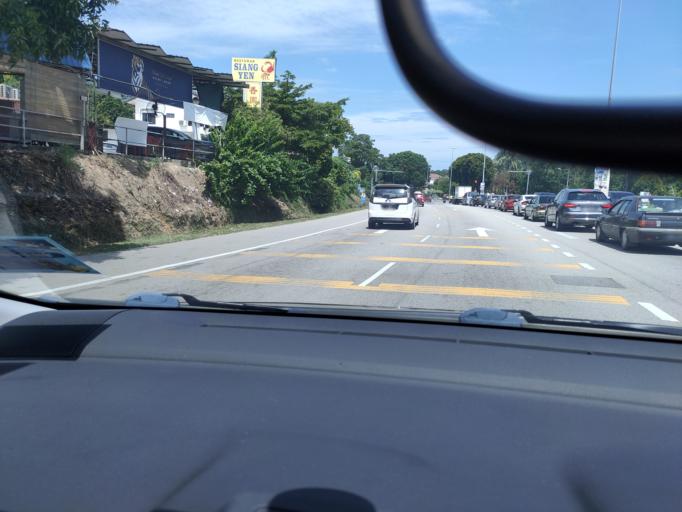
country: MY
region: Melaka
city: Batu Berendam
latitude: 2.2666
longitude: 102.2178
